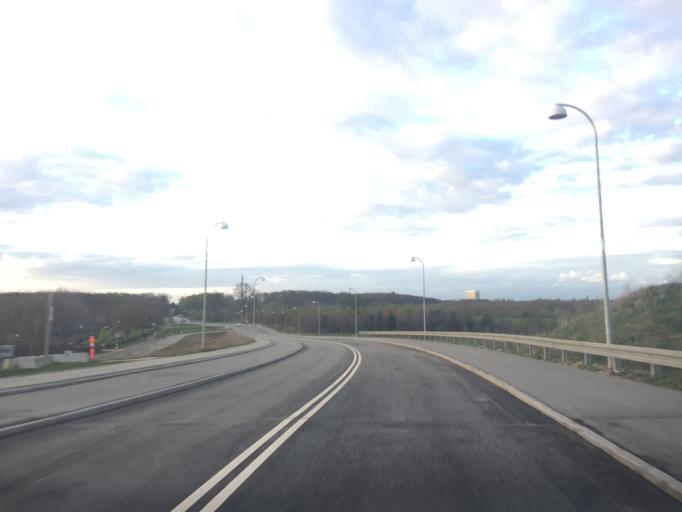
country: DK
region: Capital Region
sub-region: Hvidovre Kommune
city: Hvidovre
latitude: 55.6473
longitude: 12.4446
